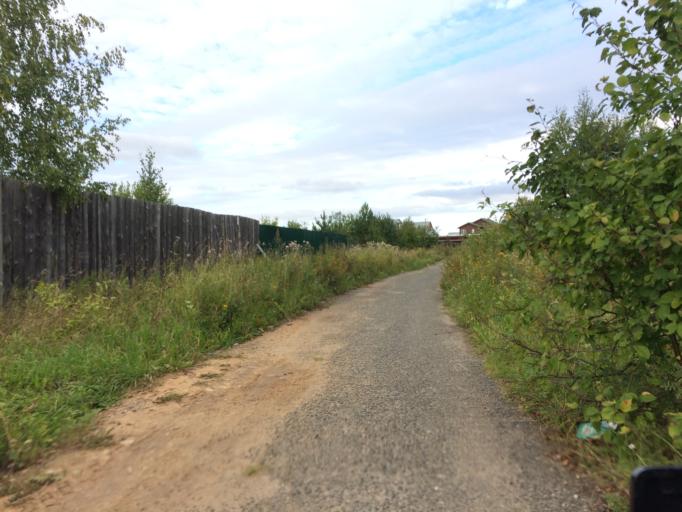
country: RU
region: Mariy-El
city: Yoshkar-Ola
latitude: 56.6603
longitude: 47.9923
